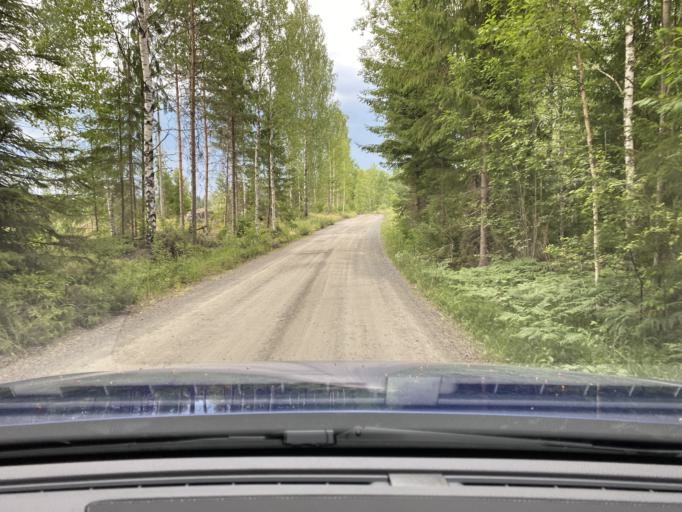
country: FI
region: Satakunta
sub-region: Rauma
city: Lappi
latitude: 61.1357
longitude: 21.9024
